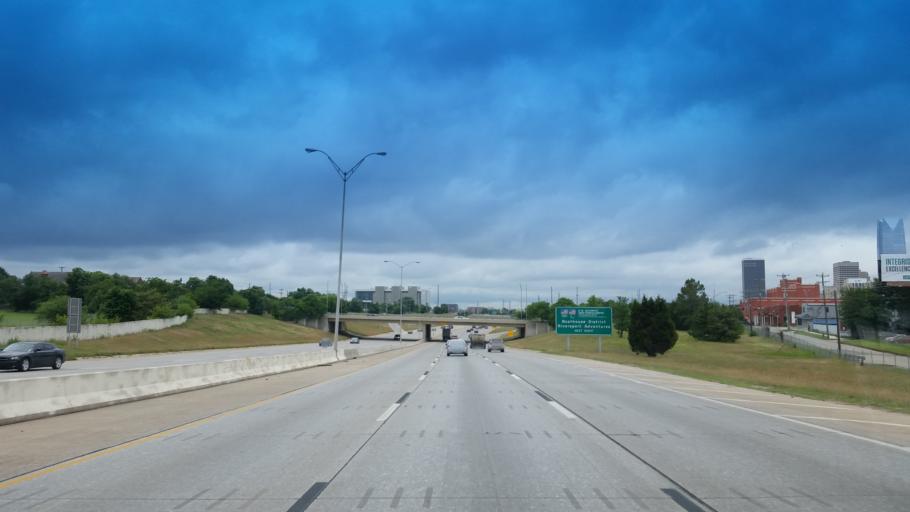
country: US
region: Oklahoma
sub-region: Oklahoma County
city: Oklahoma City
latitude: 35.4846
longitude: -97.5108
